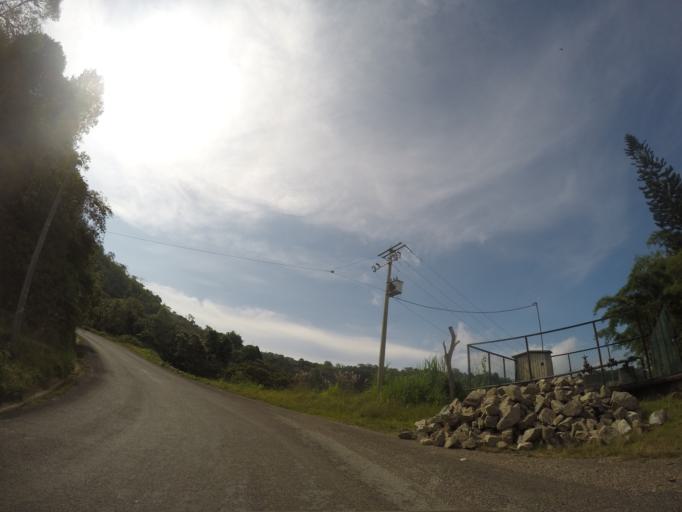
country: MX
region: Oaxaca
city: Pluma Hidalgo
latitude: 15.9332
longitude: -96.4305
